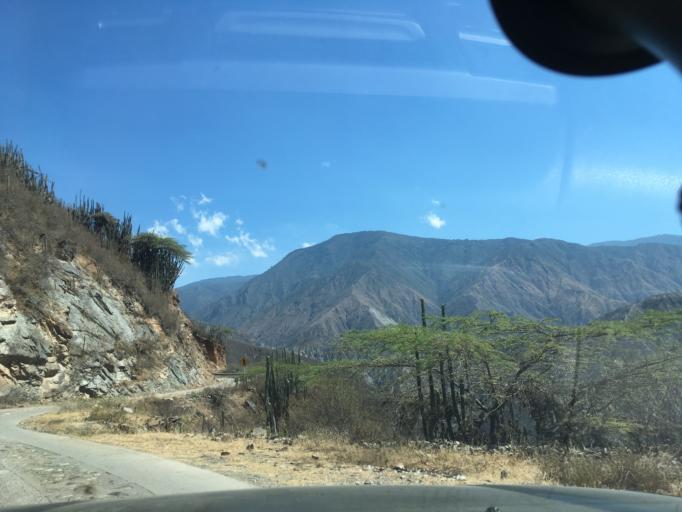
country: CO
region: Santander
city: Aratoca
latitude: 6.7673
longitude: -72.9829
